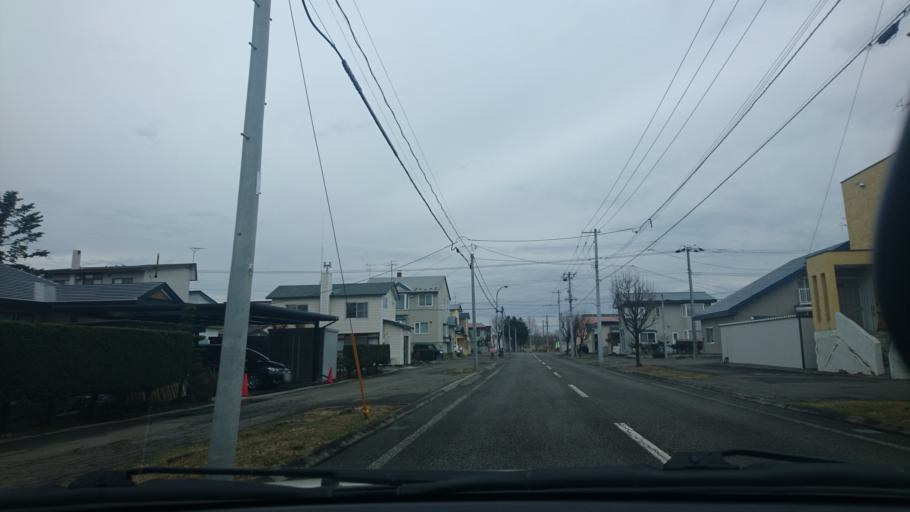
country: JP
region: Hokkaido
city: Obihiro
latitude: 42.9338
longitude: 143.1942
